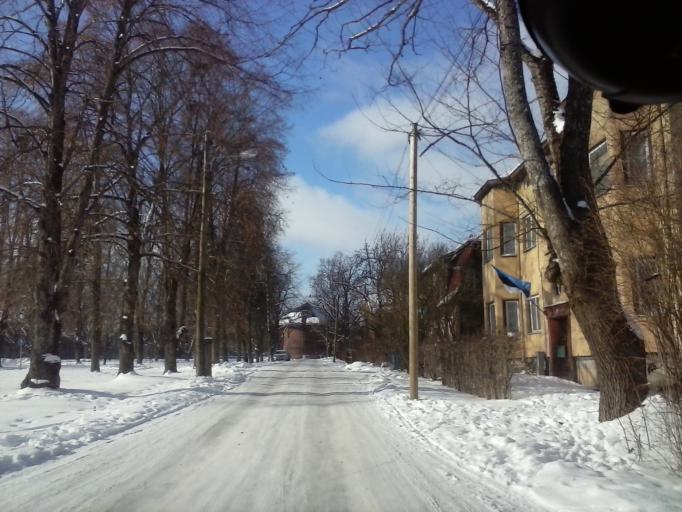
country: EE
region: Viljandimaa
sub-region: Viljandi linn
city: Viljandi
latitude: 58.3686
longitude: 25.6048
